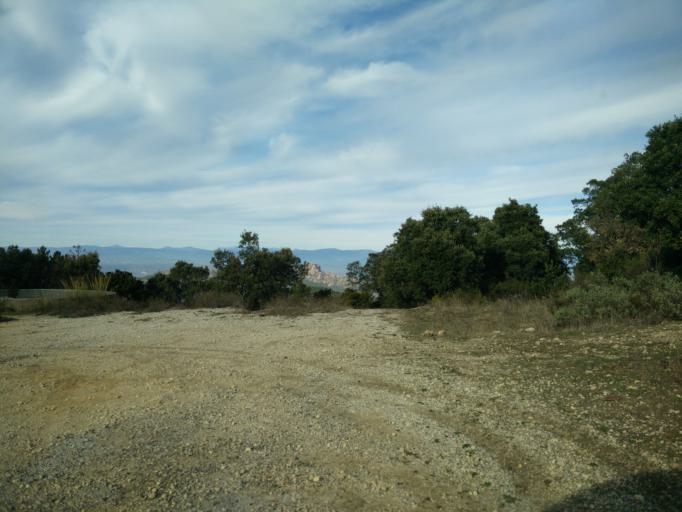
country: FR
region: Provence-Alpes-Cote d'Azur
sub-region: Departement du Var
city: Roquebrune-sur-Argens
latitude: 43.4039
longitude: 6.6219
